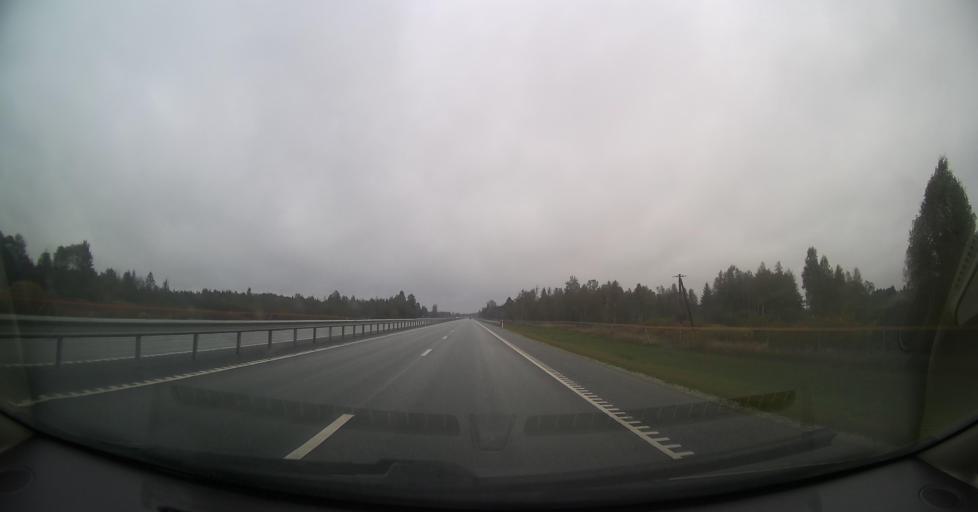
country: EE
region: Harju
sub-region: Anija vald
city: Kehra
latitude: 59.1412
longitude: 25.2514
